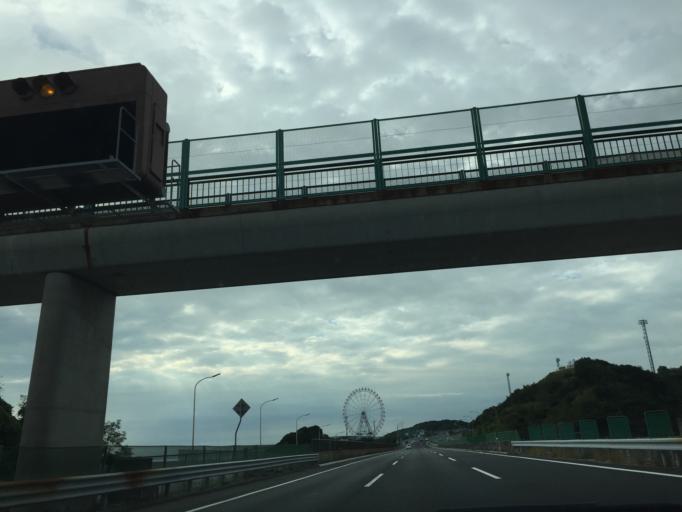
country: JP
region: Hyogo
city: Akashi
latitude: 34.5896
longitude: 135.0114
